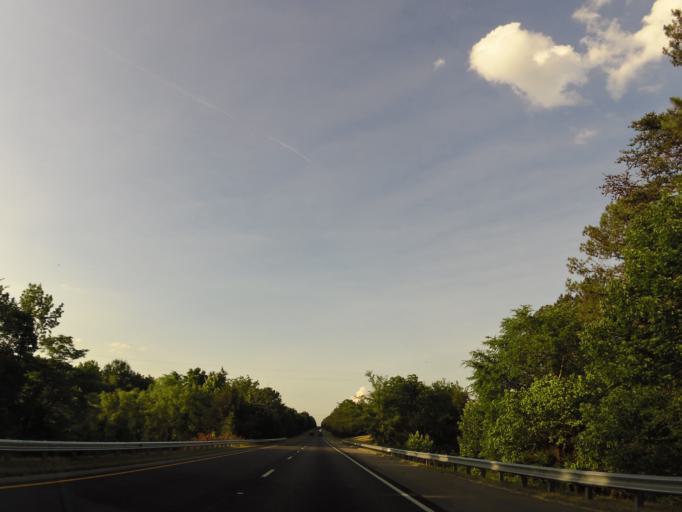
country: US
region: Alabama
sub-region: DeKalb County
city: Fort Payne
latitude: 34.3925
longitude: -85.7877
